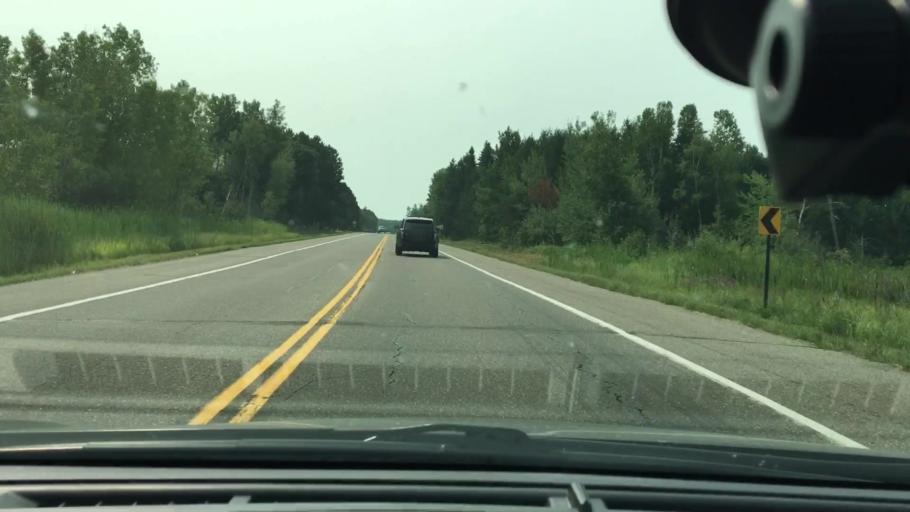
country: US
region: Minnesota
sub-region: Crow Wing County
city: Brainerd
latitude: 46.3964
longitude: -94.2234
